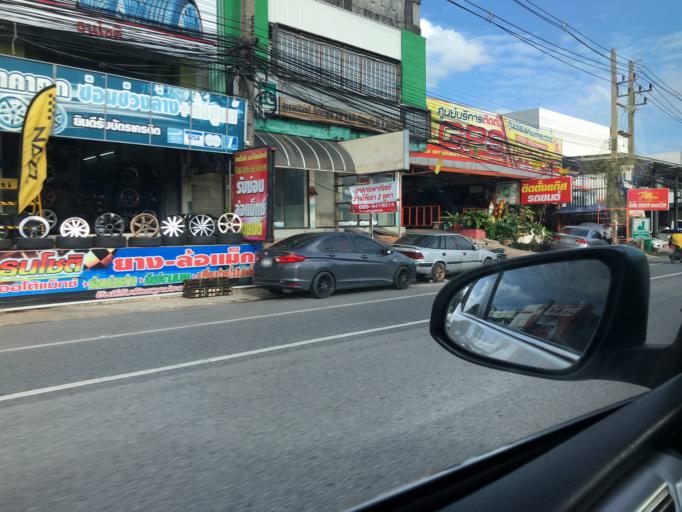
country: TH
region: Phuket
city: Ban Ko Kaeo
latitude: 7.9242
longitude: 98.3960
